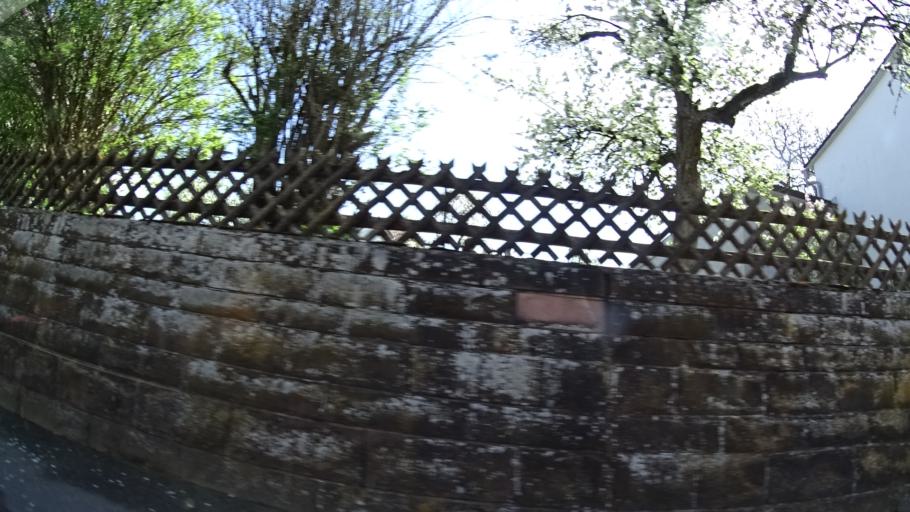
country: DE
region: Baden-Wuerttemberg
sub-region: Karlsruhe Region
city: Ebhausen
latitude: 48.6040
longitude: 8.6626
